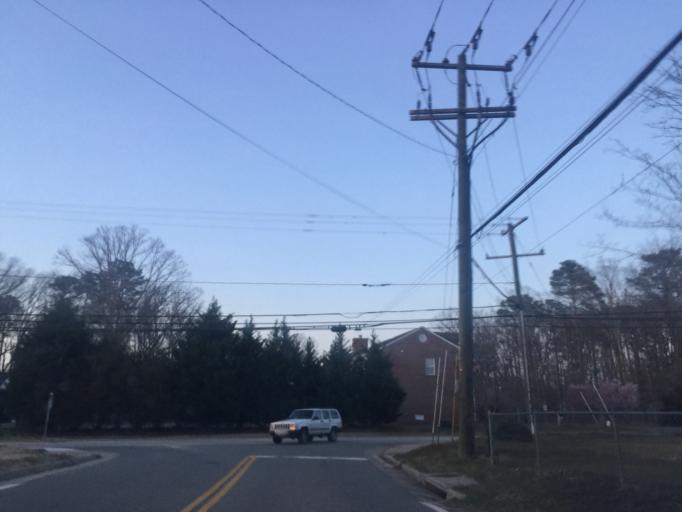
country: US
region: Virginia
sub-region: City of Newport News
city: Newport News
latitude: 37.0761
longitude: -76.5082
